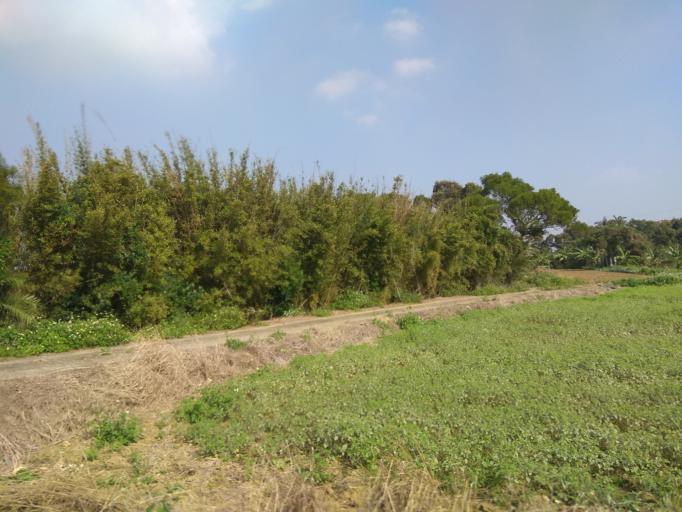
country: TW
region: Taiwan
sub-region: Hsinchu
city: Zhubei
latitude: 25.0032
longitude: 121.0515
